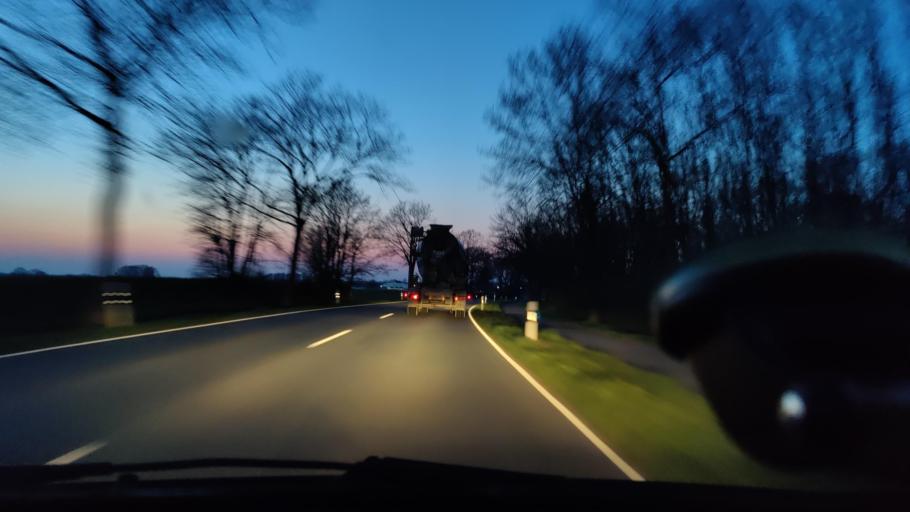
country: DE
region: North Rhine-Westphalia
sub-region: Regierungsbezirk Dusseldorf
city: Sonsbeck
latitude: 51.5938
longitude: 6.3986
